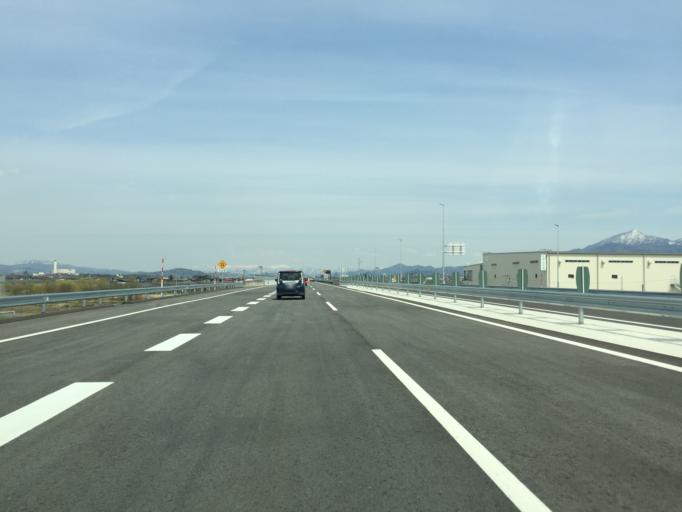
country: JP
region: Yamagata
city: Tendo
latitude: 38.4092
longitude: 140.3469
